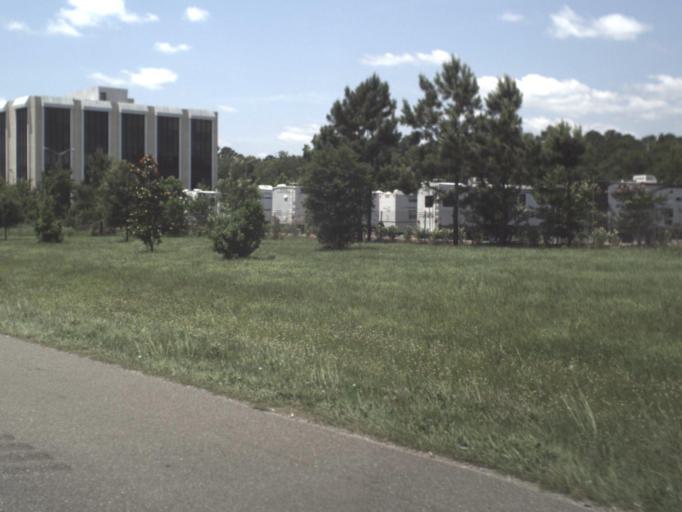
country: US
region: Florida
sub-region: Duval County
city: Jacksonville
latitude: 30.4191
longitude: -81.6570
